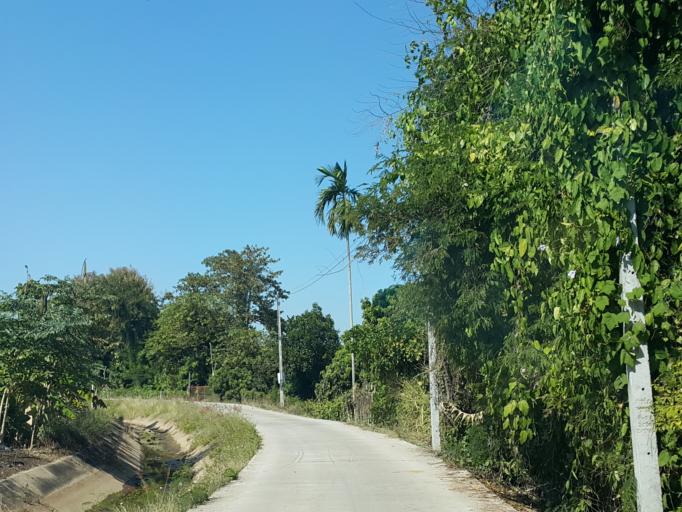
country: TH
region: Chiang Mai
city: San Sai
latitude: 18.8730
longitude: 98.9840
